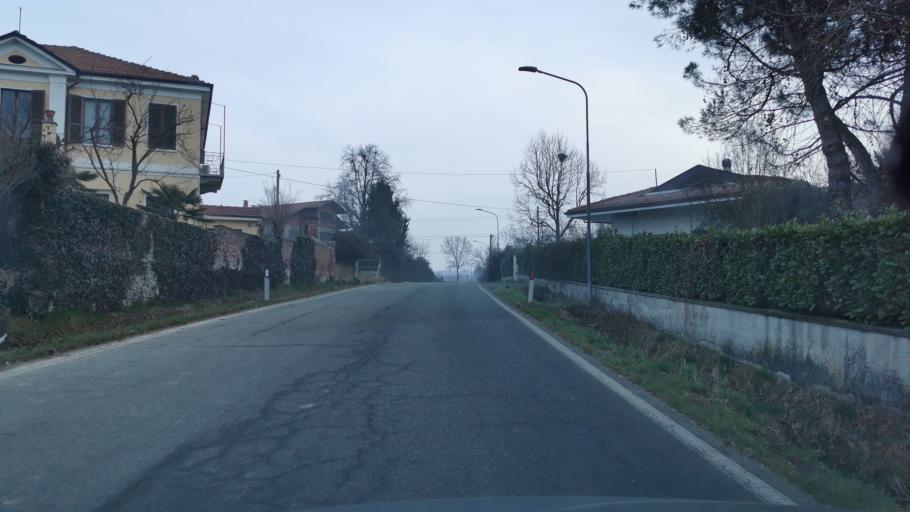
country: IT
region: Piedmont
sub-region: Provincia di Torino
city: San Giorgio Canavese
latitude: 45.3422
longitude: 7.8063
